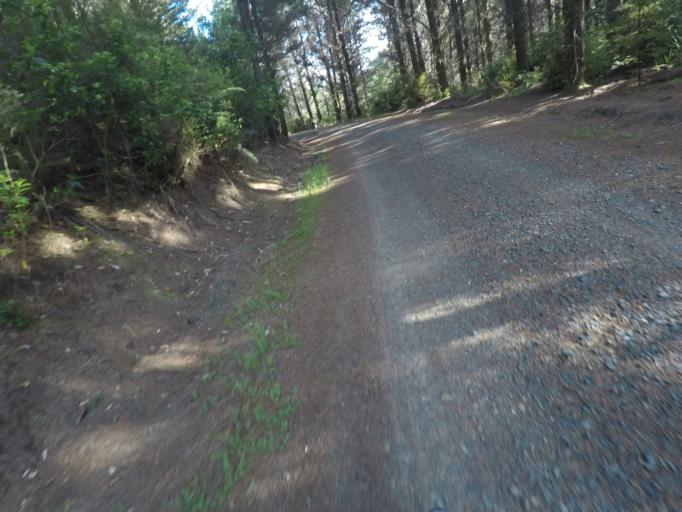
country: NZ
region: Auckland
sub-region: Auckland
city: Muriwai Beach
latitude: -36.7429
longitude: 174.5759
